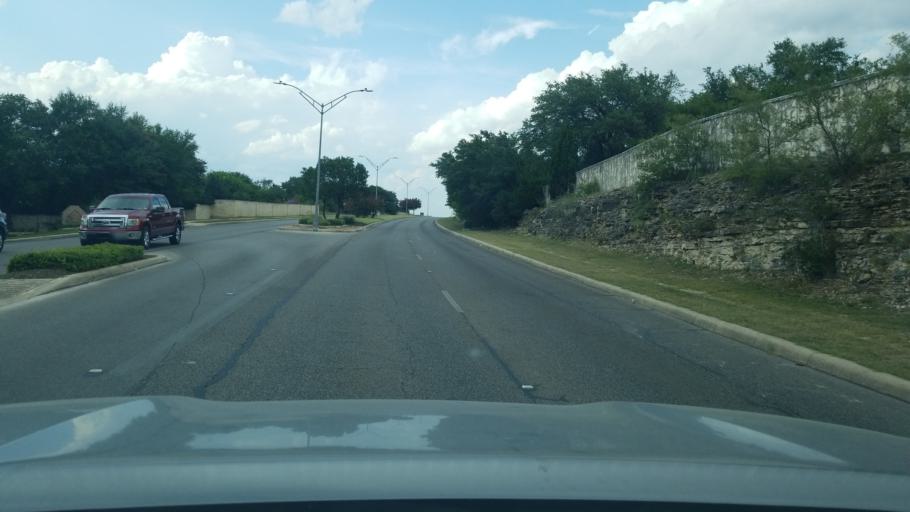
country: US
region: Texas
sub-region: Bexar County
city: Timberwood Park
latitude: 29.6551
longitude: -98.4808
